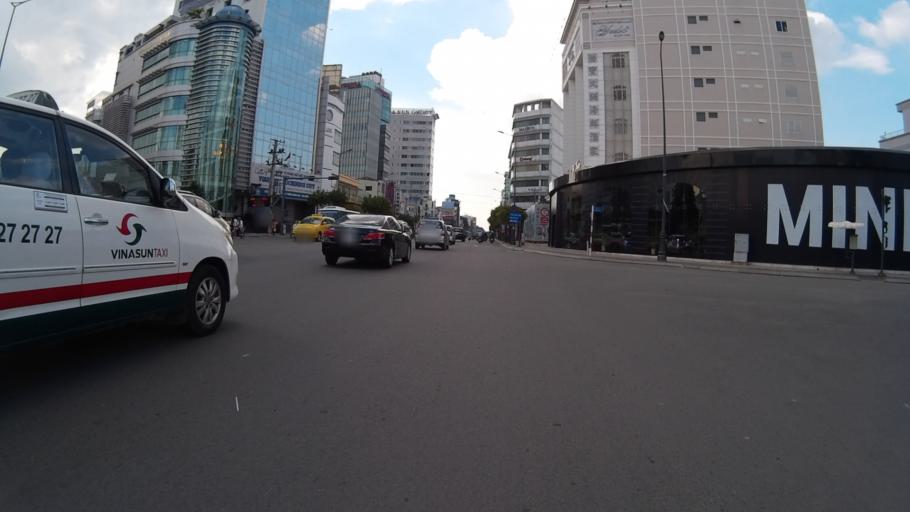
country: VN
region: Ho Chi Minh City
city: Quan Phu Nhuan
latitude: 10.7955
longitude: 106.6761
